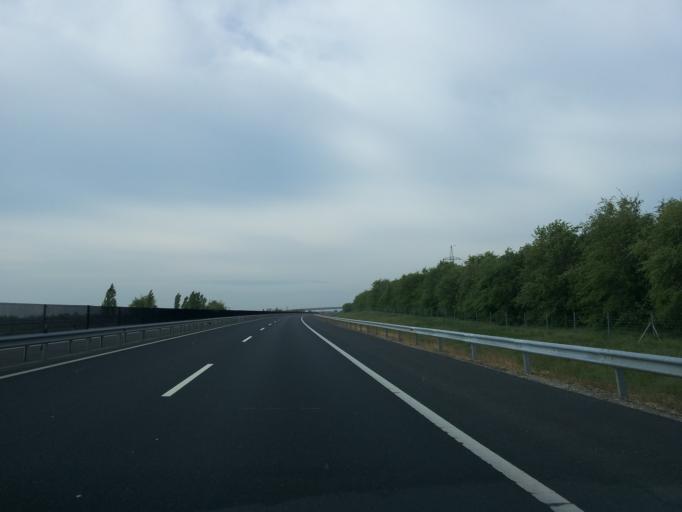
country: HU
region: Fejer
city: Ivancsa
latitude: 47.1950
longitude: 18.8156
